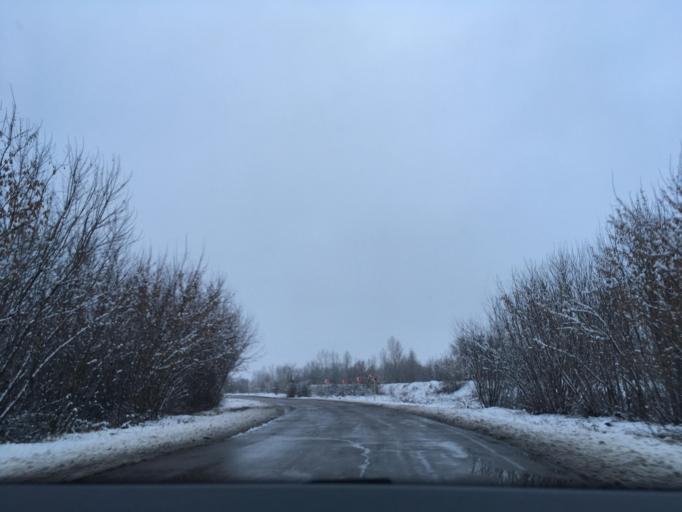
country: RU
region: Voronezj
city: Mitrofanovka
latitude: 50.1286
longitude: 39.9953
